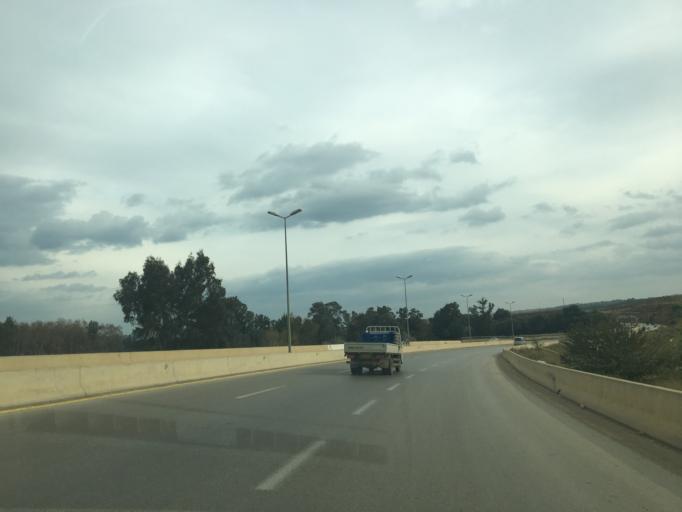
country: DZ
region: Tipaza
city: Tipasa
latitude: 36.5674
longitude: 2.3975
